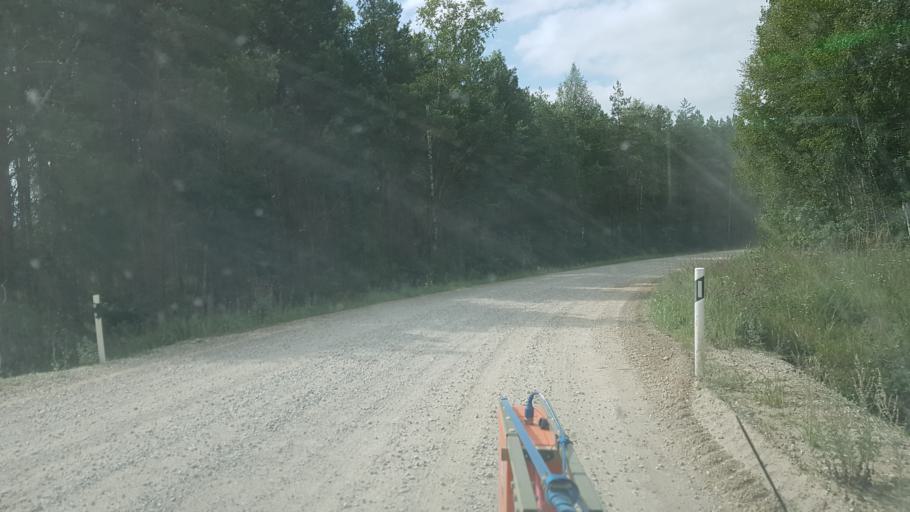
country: EE
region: Paernumaa
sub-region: Audru vald
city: Audru
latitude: 58.5167
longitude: 24.4045
